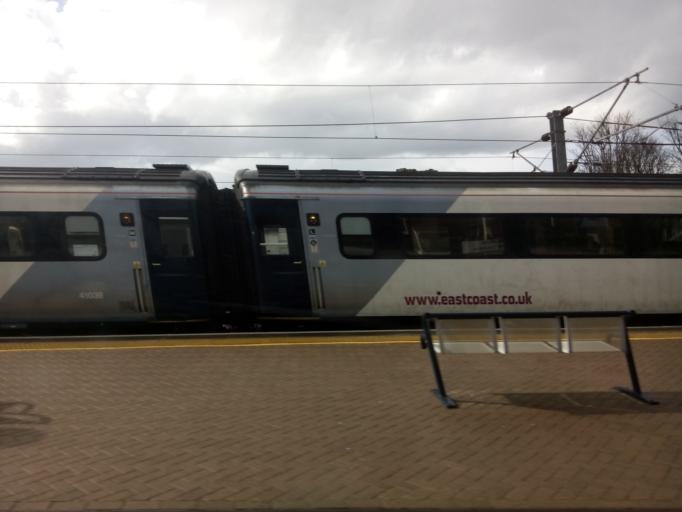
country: GB
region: England
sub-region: Northumberland
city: Berwick-Upon-Tweed
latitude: 55.7742
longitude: -2.0107
